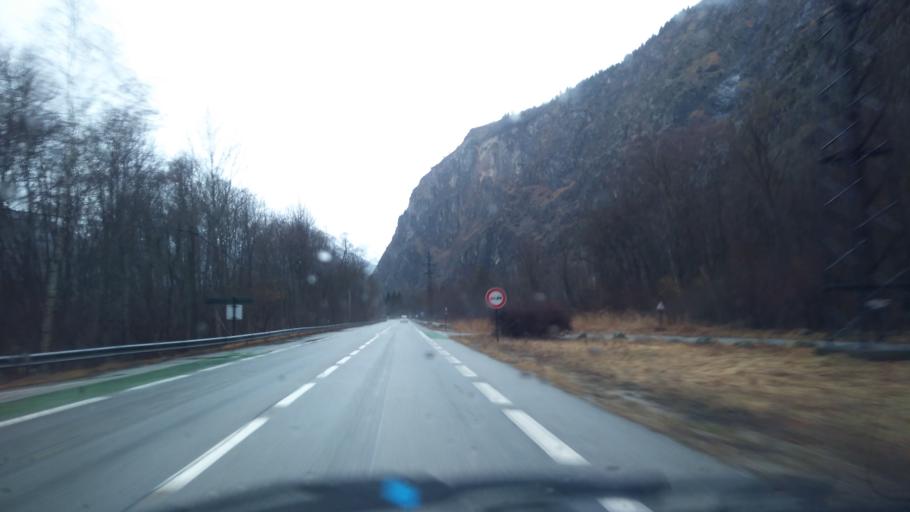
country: FR
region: Rhone-Alpes
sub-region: Departement de l'Isere
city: Huez
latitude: 45.0432
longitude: 6.0588
